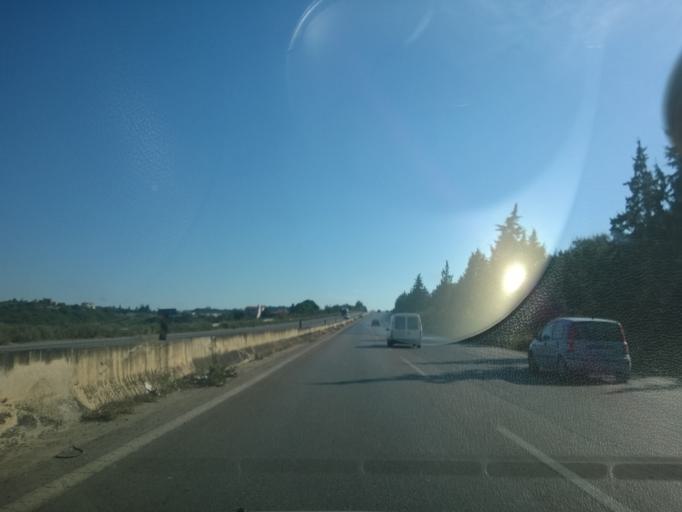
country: GR
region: Central Macedonia
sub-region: Nomos Thessalonikis
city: Kardia
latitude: 40.4786
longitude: 22.9928
